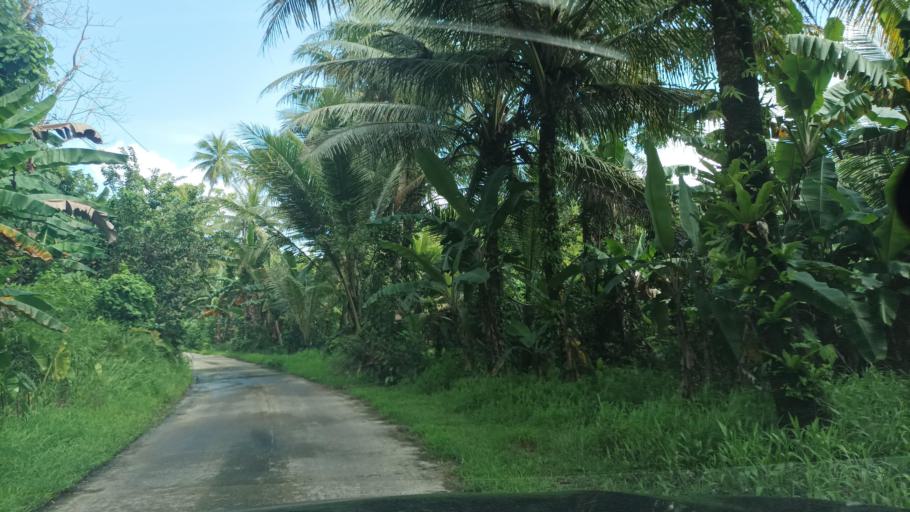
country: FM
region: Pohnpei
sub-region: Sokehs Municipality
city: Palikir - National Government Center
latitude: 6.9410
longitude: 158.1658
